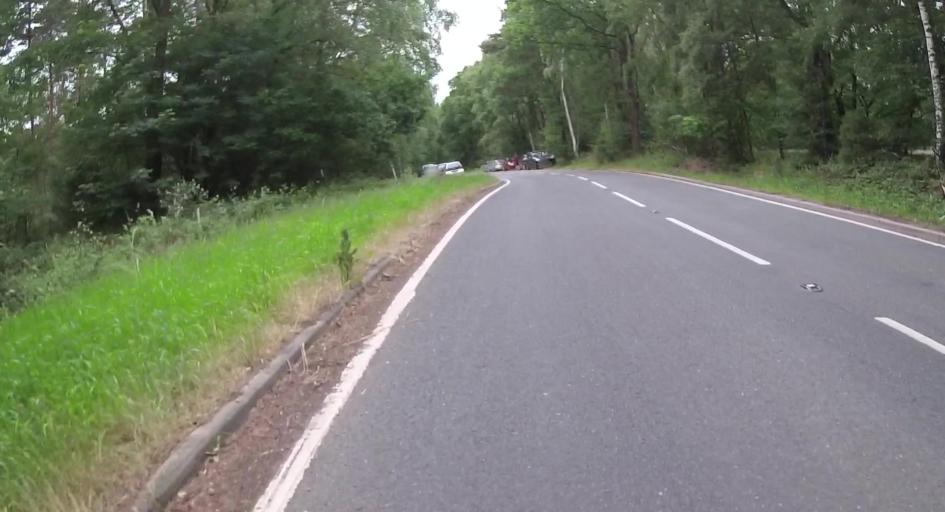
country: GB
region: England
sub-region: Surrey
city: Hale
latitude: 51.2497
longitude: -0.8068
